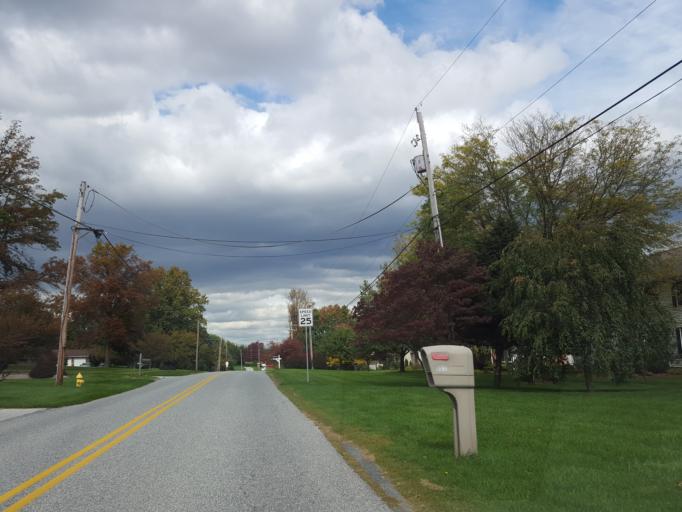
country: US
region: Pennsylvania
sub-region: York County
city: Spry
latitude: 39.9294
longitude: -76.6725
